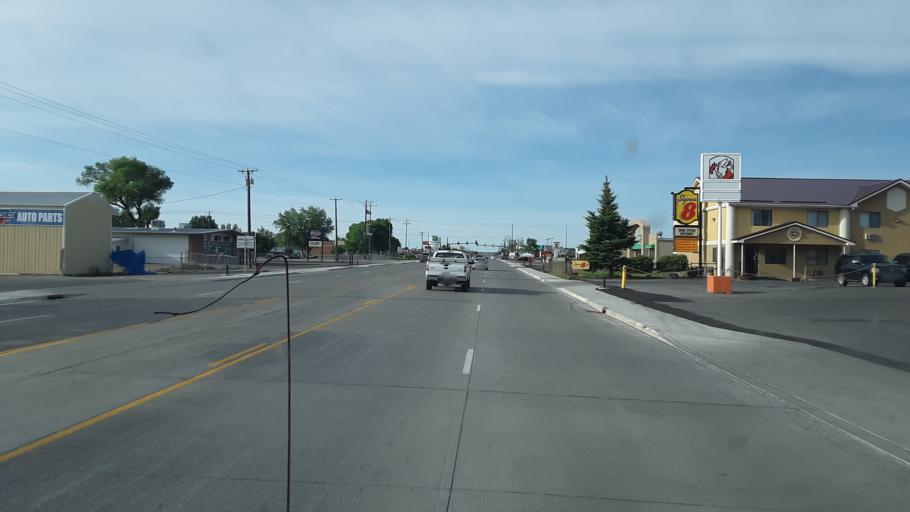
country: US
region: Wyoming
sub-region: Fremont County
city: Riverton
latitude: 43.0370
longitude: -108.3807
